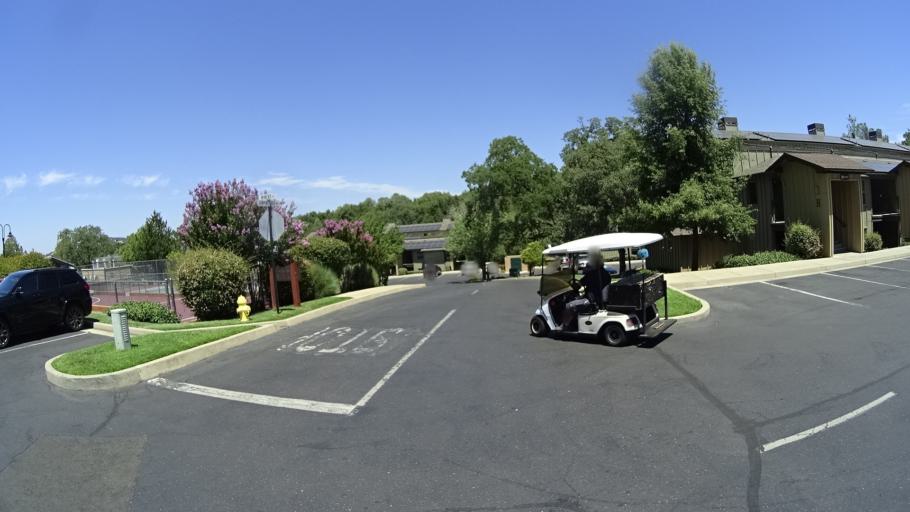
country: US
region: California
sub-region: Calaveras County
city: Angels Camp
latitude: 38.0698
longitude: -120.5540
